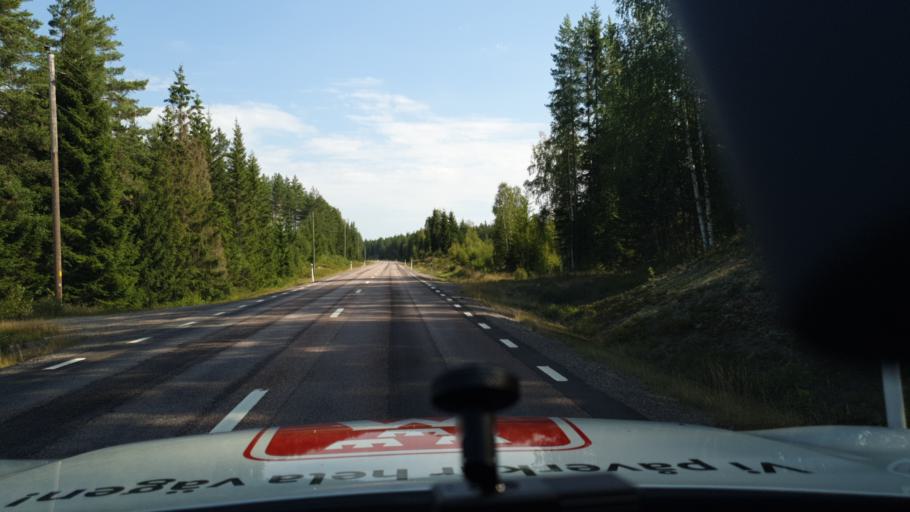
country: SE
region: Vaermland
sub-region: Hagfors Kommun
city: Ekshaerad
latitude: 60.4471
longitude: 13.2800
